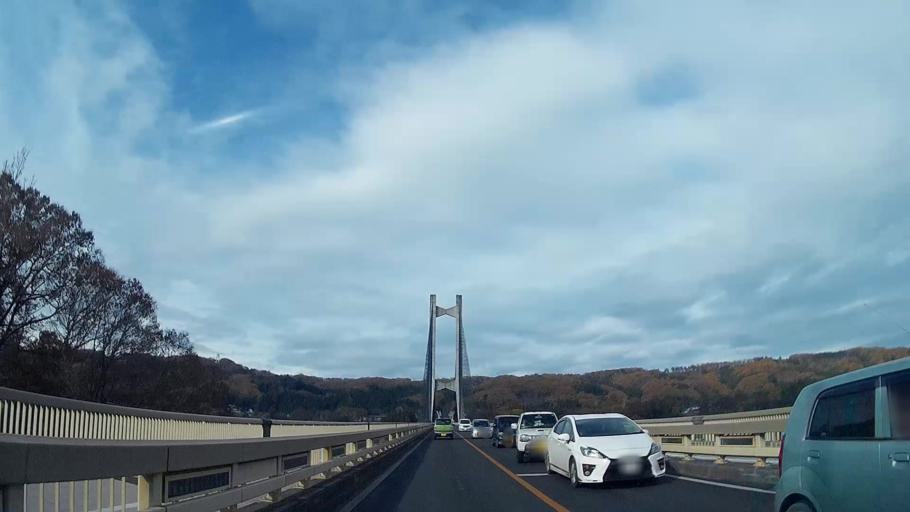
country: JP
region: Saitama
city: Chichibu
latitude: 36.0017
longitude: 139.0755
